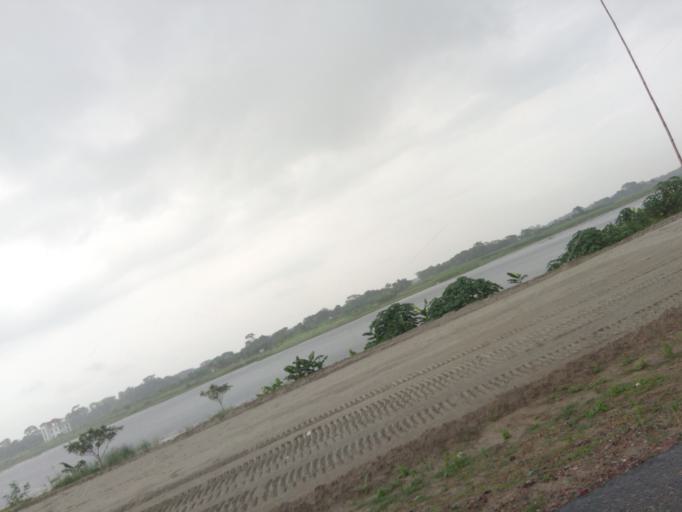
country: BD
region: Dhaka
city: Char Bhadrasan
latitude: 23.3703
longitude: 90.0802
